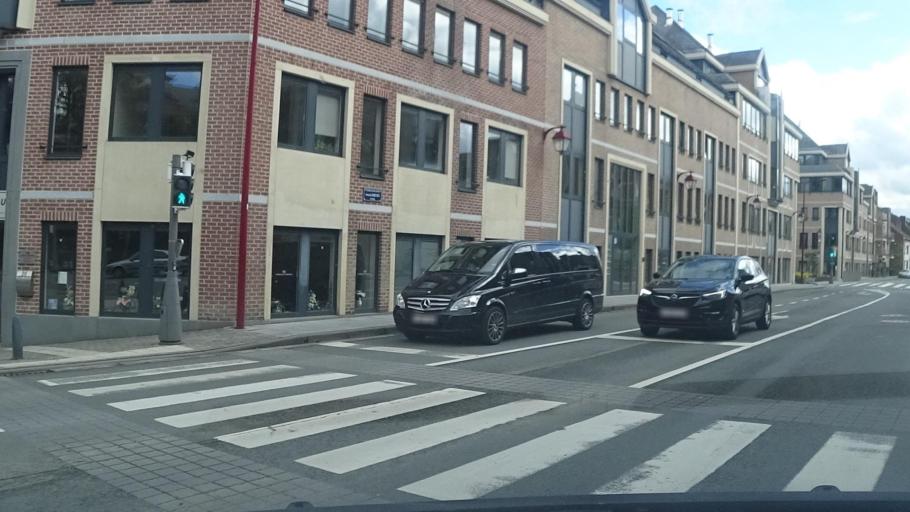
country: BE
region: Wallonia
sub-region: Province du Brabant Wallon
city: Ottignies
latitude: 50.6659
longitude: 4.5669
